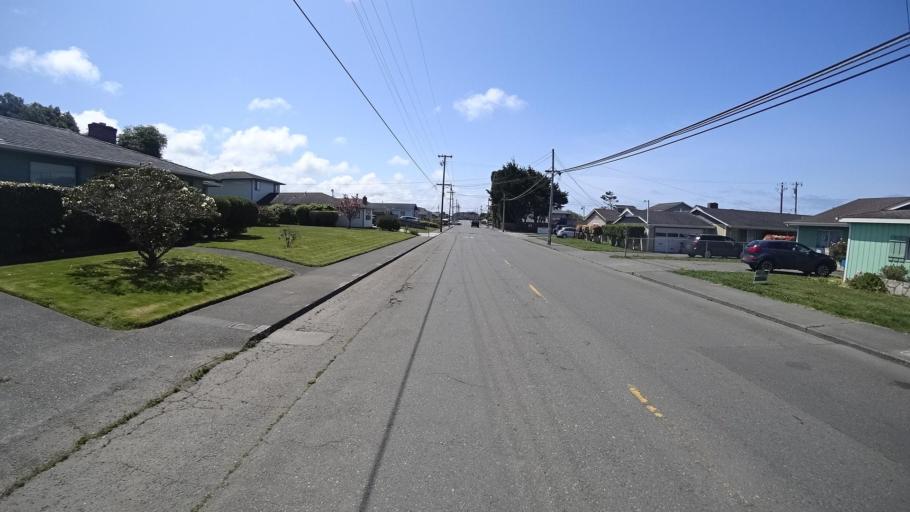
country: US
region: California
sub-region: Humboldt County
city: Bayview
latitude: 40.7830
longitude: -124.1818
